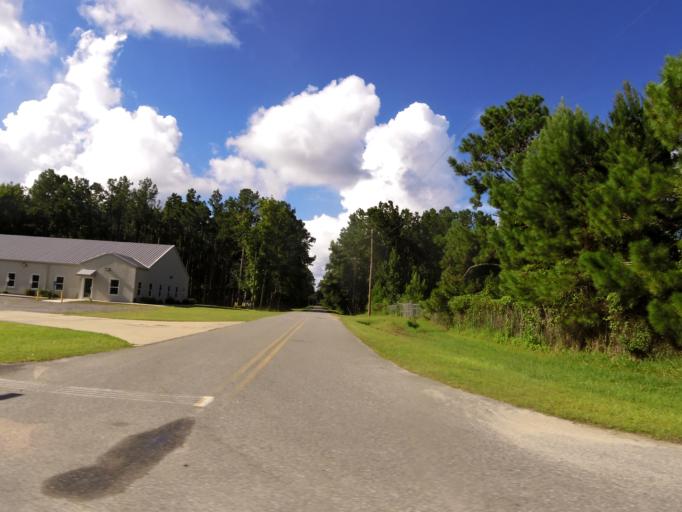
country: US
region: Georgia
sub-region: Camden County
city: Woodbine
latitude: 30.9621
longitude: -81.7260
